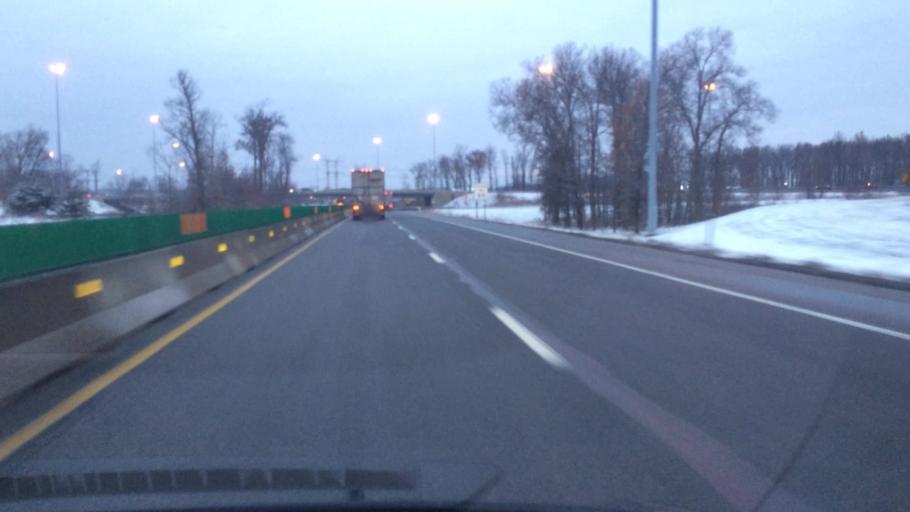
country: US
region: Ohio
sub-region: Summit County
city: Richfield
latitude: 41.2695
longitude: -81.6198
